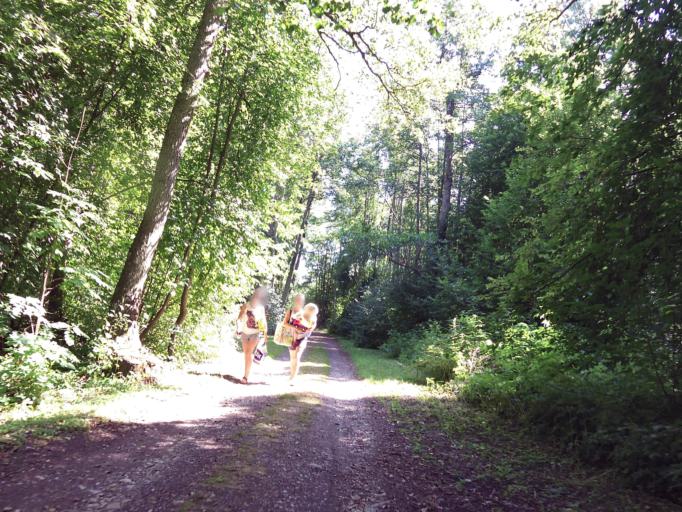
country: EE
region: Hiiumaa
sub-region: Kaerdla linn
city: Kardla
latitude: 58.9333
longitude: 22.3896
